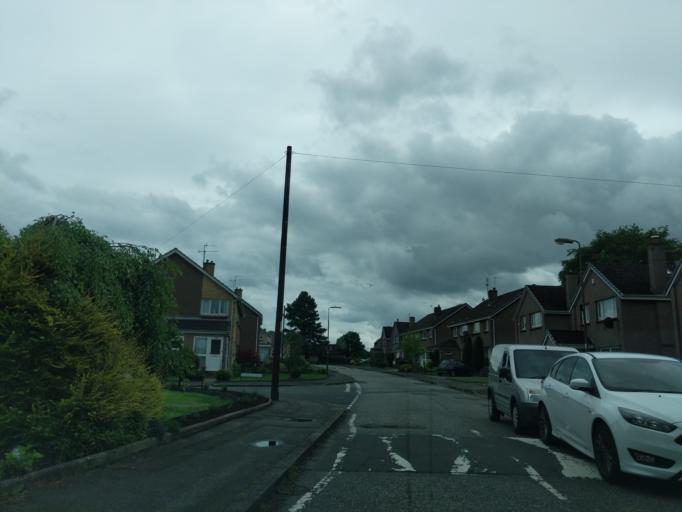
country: GB
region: Scotland
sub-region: Edinburgh
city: Colinton
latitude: 55.9502
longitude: -3.2890
